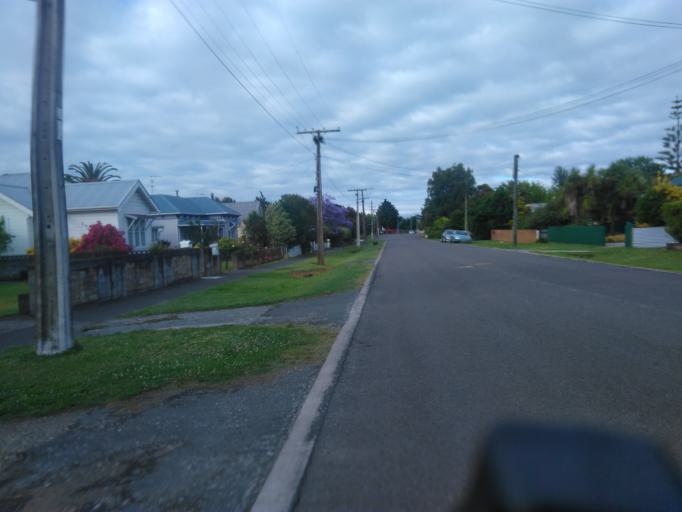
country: NZ
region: Gisborne
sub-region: Gisborne District
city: Gisborne
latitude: -38.6489
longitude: 178.0222
